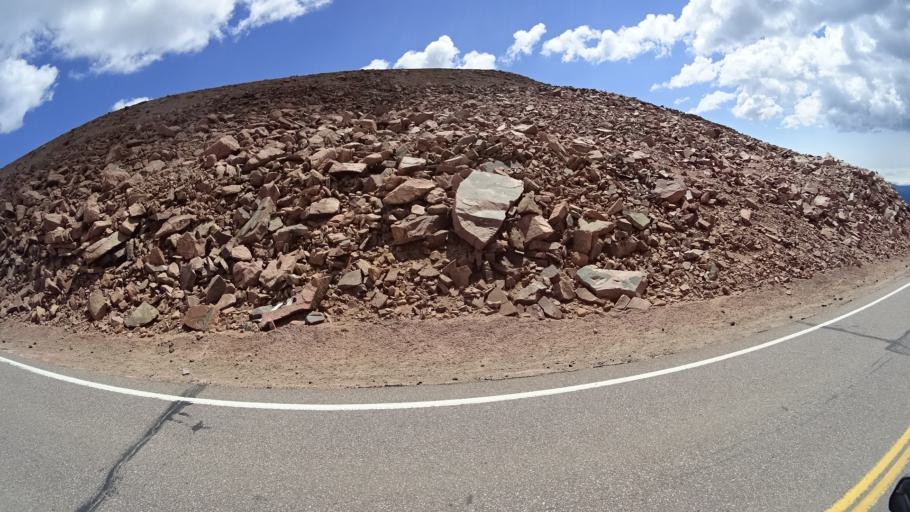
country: US
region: Colorado
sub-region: El Paso County
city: Cascade-Chipita Park
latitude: 38.8404
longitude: -105.0470
